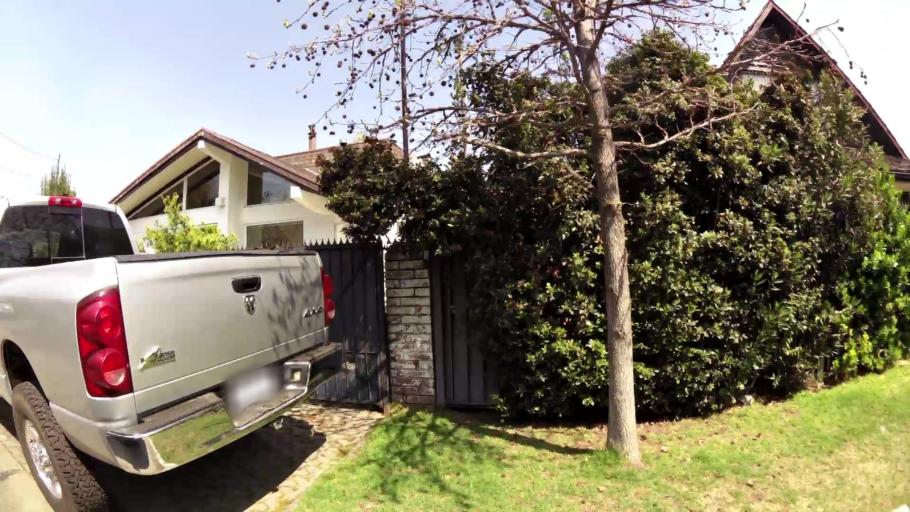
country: CL
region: Santiago Metropolitan
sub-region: Provincia de Santiago
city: Villa Presidente Frei, Nunoa, Santiago, Chile
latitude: -33.3884
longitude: -70.5854
